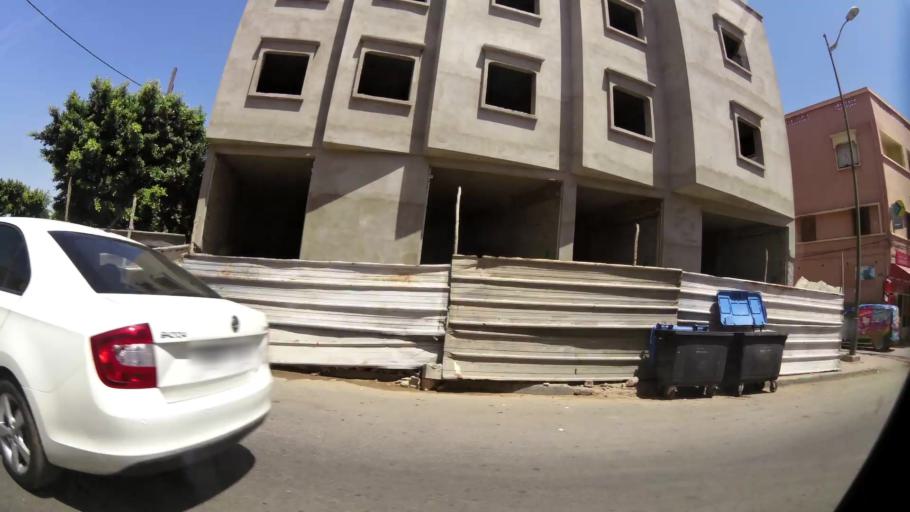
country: MA
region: Souss-Massa-Draa
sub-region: Inezgane-Ait Mellou
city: Inezgane
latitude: 30.3471
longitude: -9.4997
